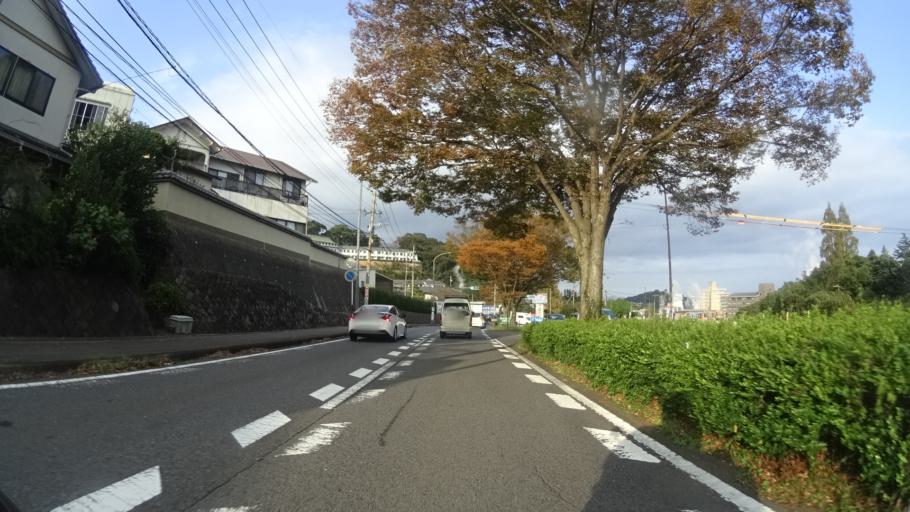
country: JP
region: Oita
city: Beppu
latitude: 33.3145
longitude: 131.4703
